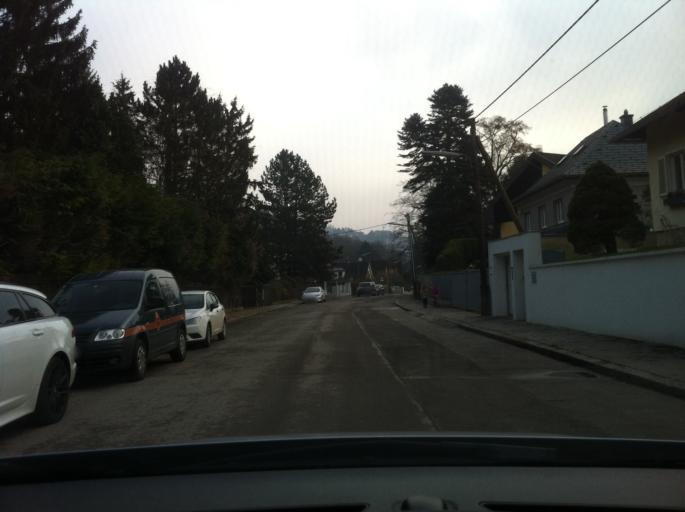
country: AT
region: Lower Austria
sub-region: Politischer Bezirk Wien-Umgebung
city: Purkersdorf
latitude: 48.2248
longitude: 16.2455
